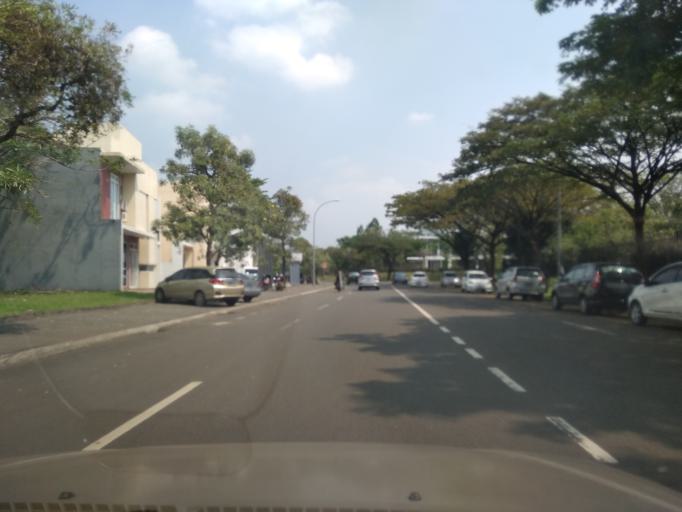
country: ID
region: West Java
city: Serpong
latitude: -6.3135
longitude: 106.6498
